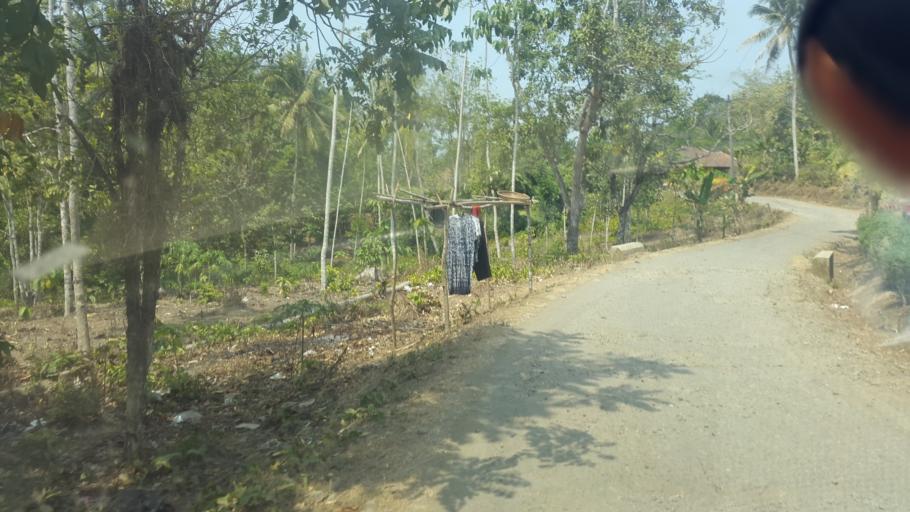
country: ID
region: West Java
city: Leuwinanggung Satu
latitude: -7.2955
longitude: 106.6429
